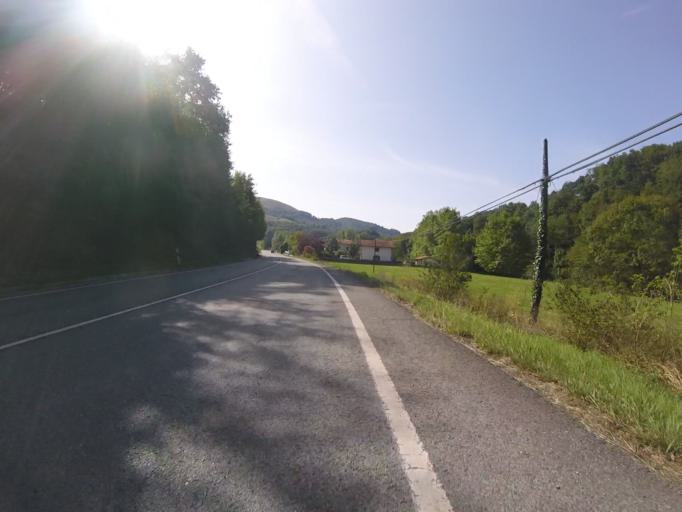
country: ES
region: Navarre
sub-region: Provincia de Navarra
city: Zugarramurdi
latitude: 43.1638
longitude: -1.4971
